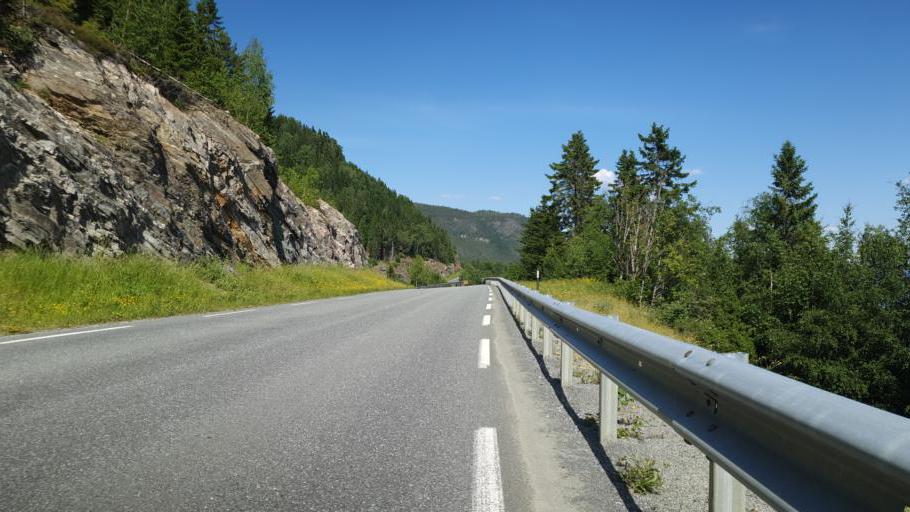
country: NO
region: Nord-Trondelag
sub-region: Leksvik
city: Leksvik
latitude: 63.6119
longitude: 10.5066
